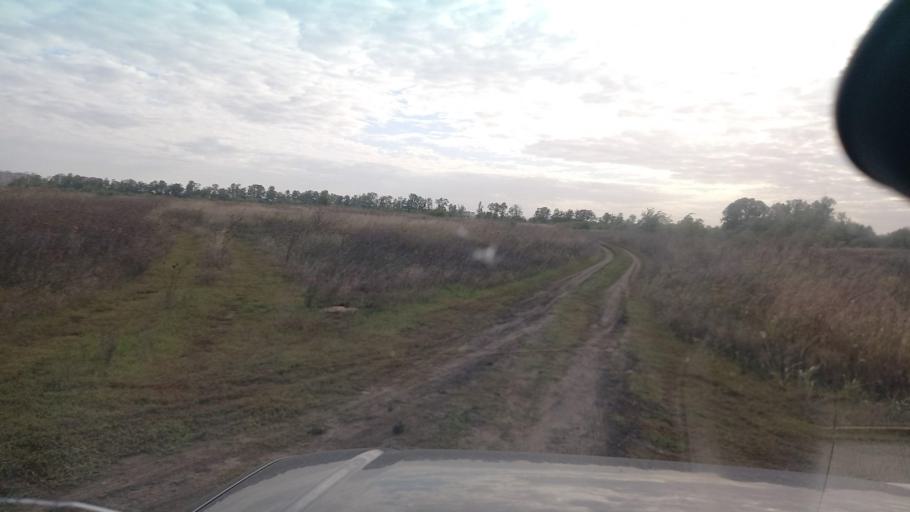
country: RU
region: Krasnodarskiy
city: Krasnodar
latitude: 45.1304
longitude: 38.9185
